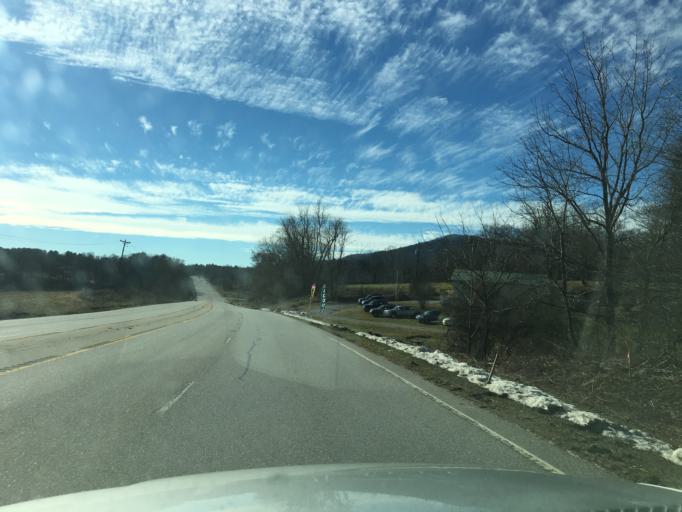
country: US
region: North Carolina
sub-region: Henderson County
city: Mills River
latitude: 35.3741
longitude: -82.5843
